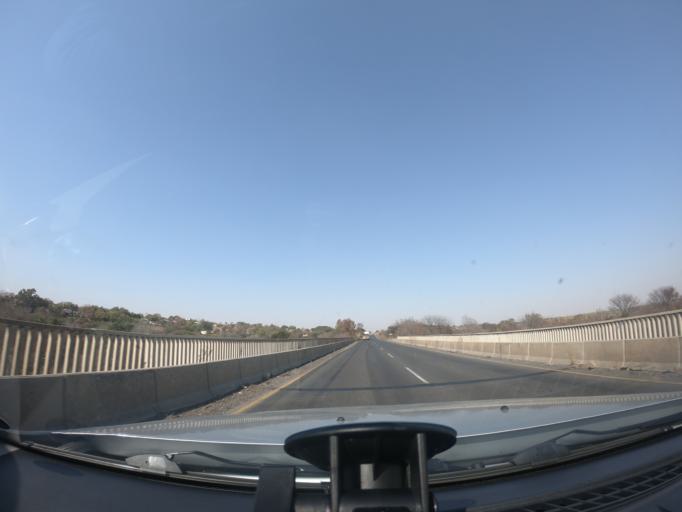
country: ZA
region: KwaZulu-Natal
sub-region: uThukela District Municipality
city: Ladysmith
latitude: -28.7417
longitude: 29.8188
